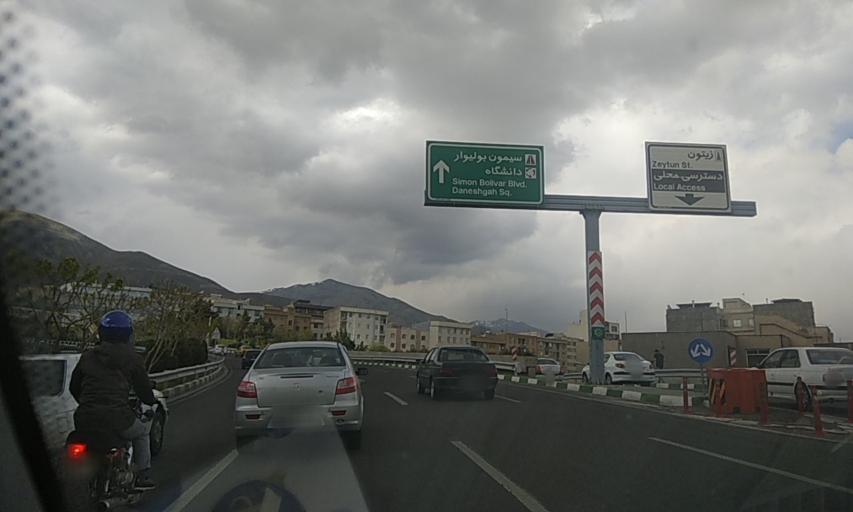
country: IR
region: Tehran
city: Tajrish
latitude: 35.7726
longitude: 51.3204
